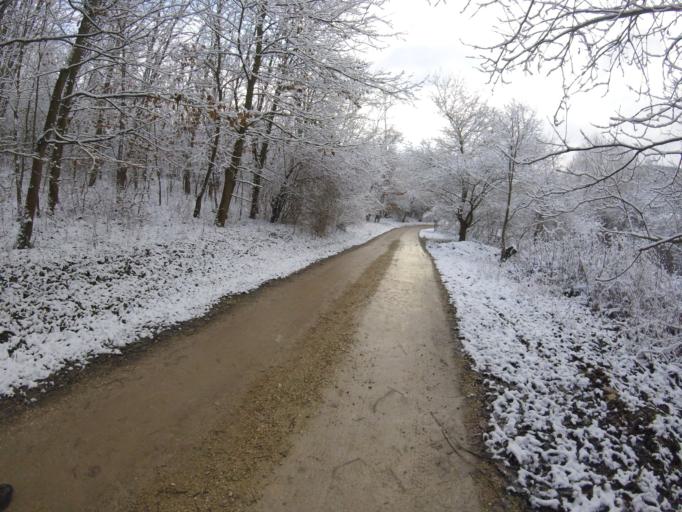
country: HU
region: Komarom-Esztergom
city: Esztergom
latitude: 47.7888
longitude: 18.7980
